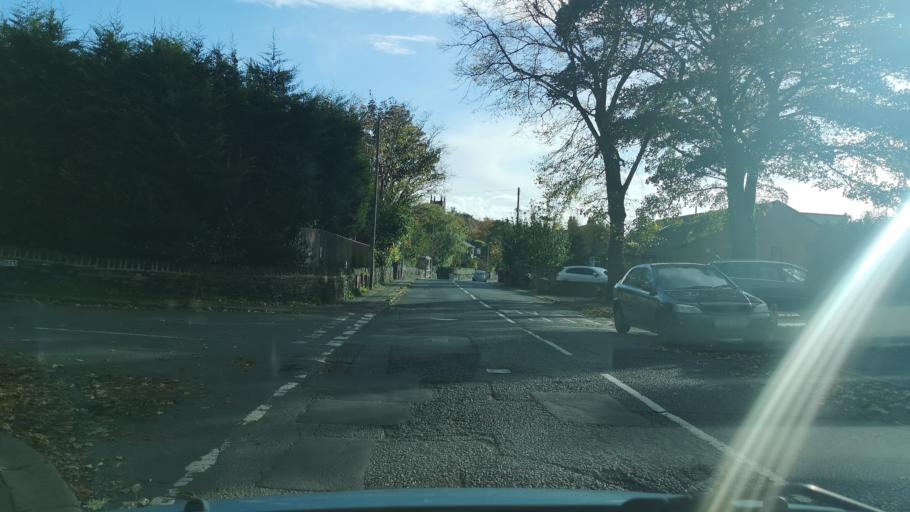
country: GB
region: England
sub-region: Kirklees
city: Batley
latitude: 53.6954
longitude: -1.6517
